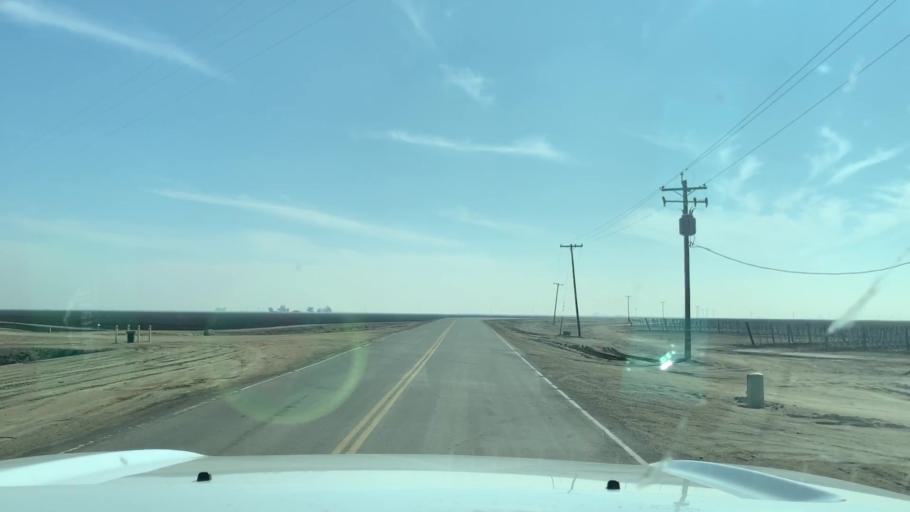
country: US
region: California
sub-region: Kern County
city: Buttonwillow
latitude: 35.4853
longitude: -119.5947
